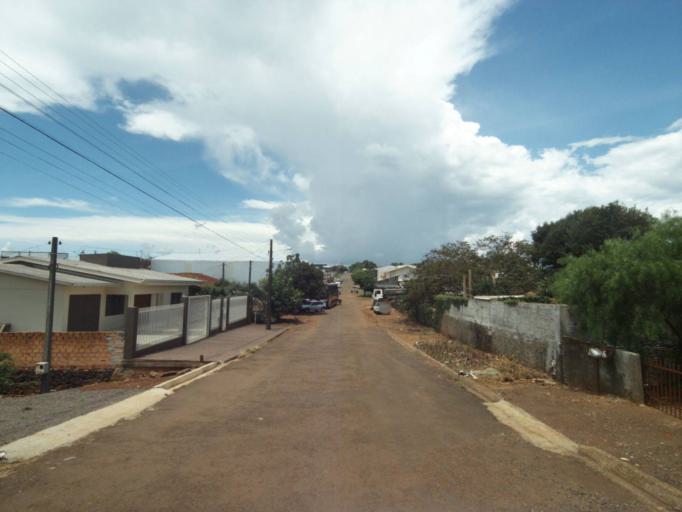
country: BR
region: Parana
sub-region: Guaraniacu
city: Guaraniacu
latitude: -25.0959
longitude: -52.8762
